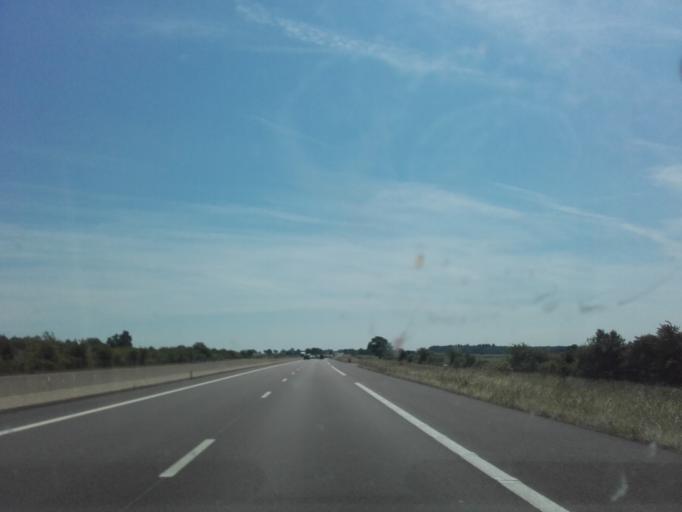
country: FR
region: Bourgogne
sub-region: Departement de la Cote-d'Or
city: Semur-en-Auxois
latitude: 47.4833
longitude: 4.1733
